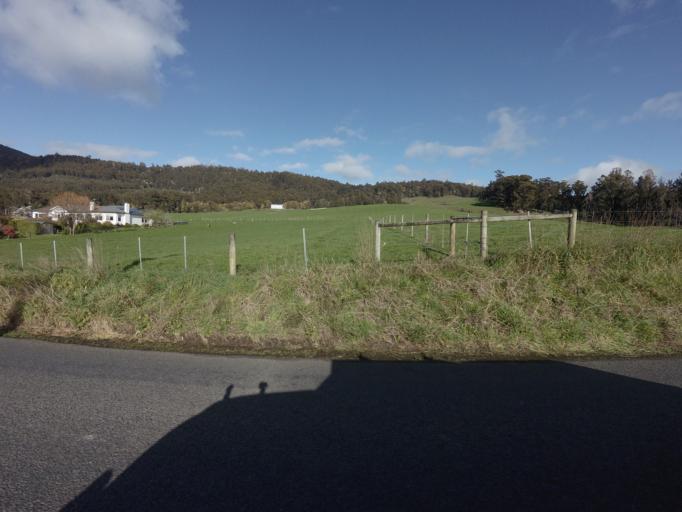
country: AU
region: Tasmania
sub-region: Huon Valley
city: Geeveston
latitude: -43.2031
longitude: 146.9652
